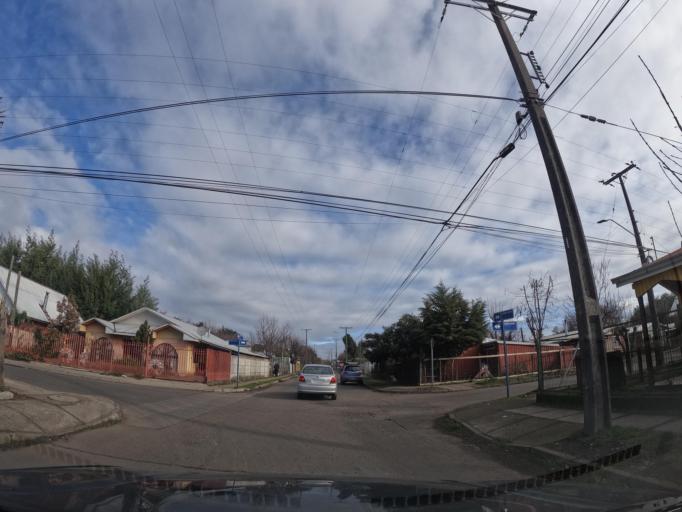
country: CL
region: Biobio
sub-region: Provincia de Nuble
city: Coihueco
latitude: -36.7000
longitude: -71.8981
